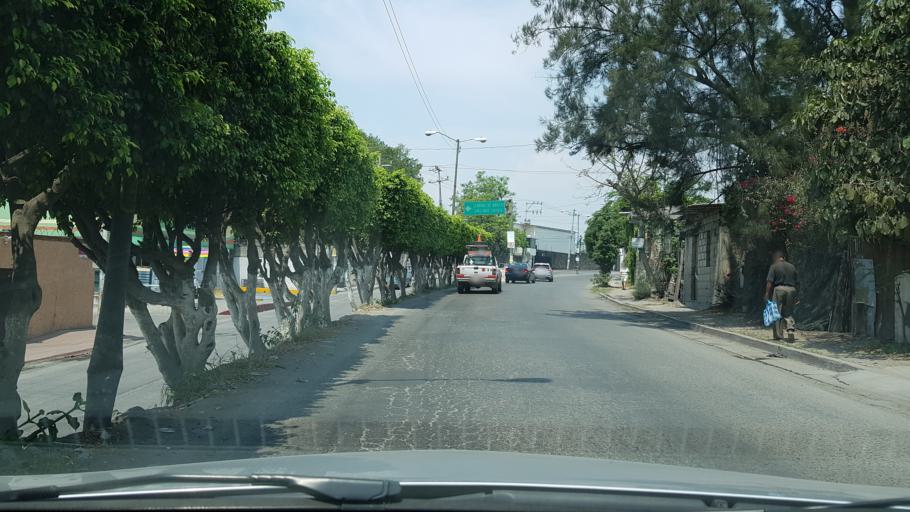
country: MX
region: Morelos
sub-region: Jiutepec
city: Jiutepec
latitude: 18.8904
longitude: -99.1740
